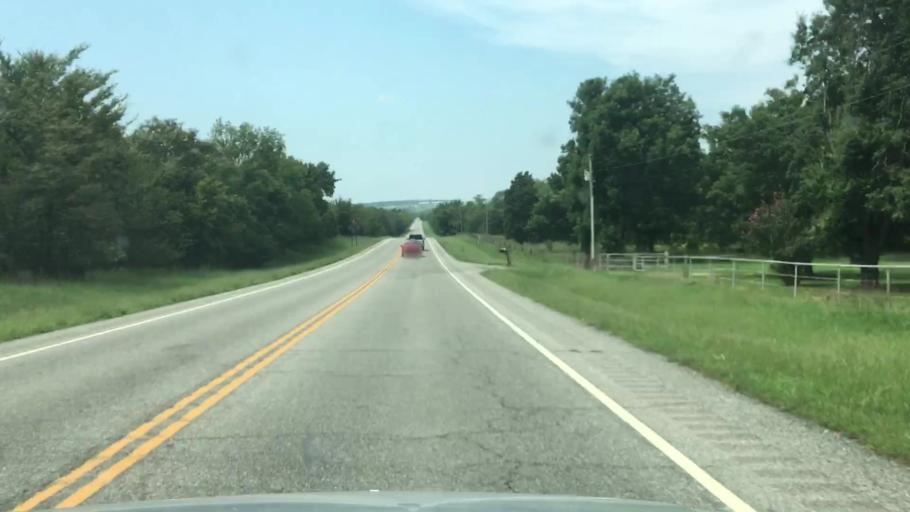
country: US
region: Oklahoma
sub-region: Muskogee County
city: Fort Gibson
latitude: 35.9369
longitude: -95.1953
